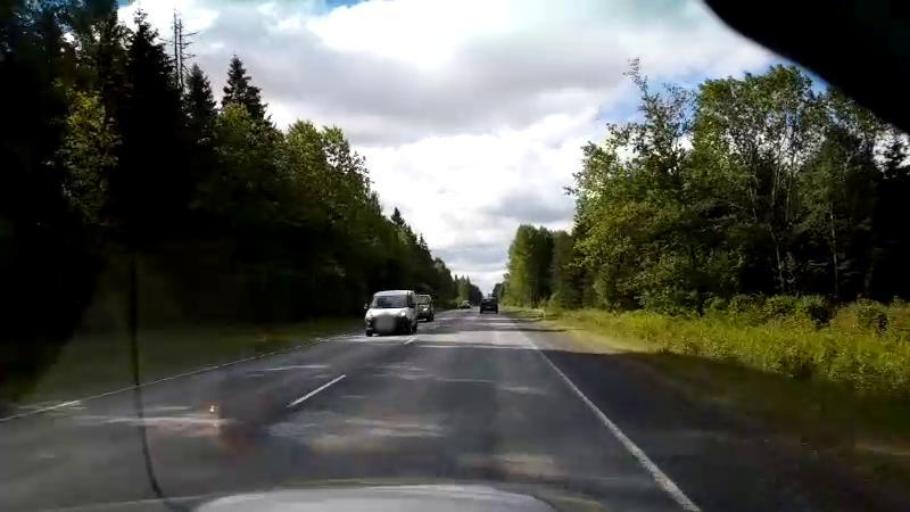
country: EE
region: Harju
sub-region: Saue linn
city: Saue
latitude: 59.2146
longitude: 24.4957
